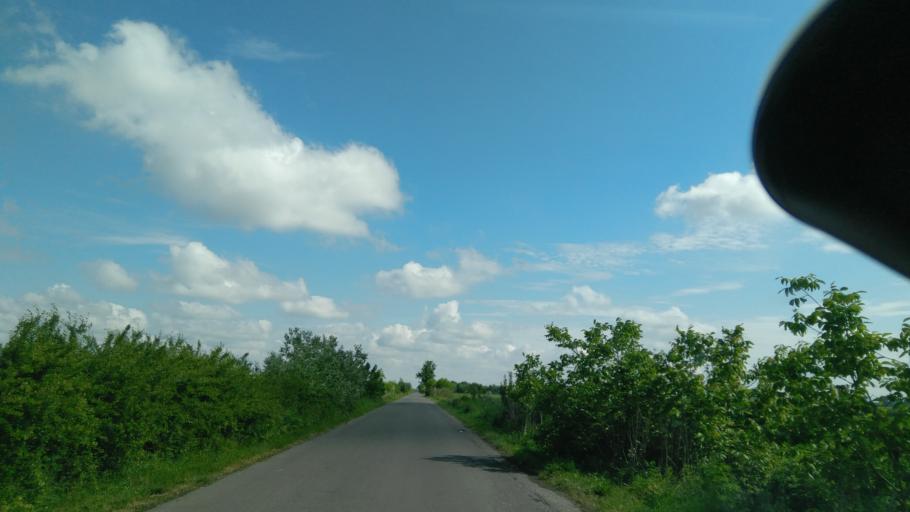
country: HU
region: Bekes
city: Bekes
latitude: 46.8022
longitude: 21.1432
